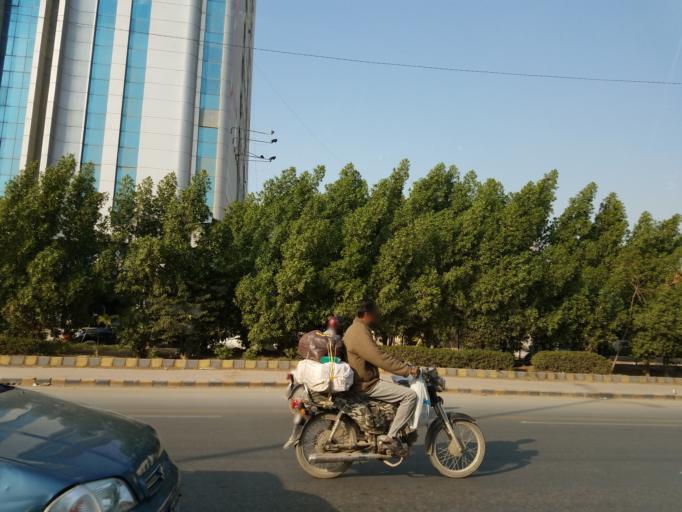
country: PK
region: Sindh
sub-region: Karachi District
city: Karachi
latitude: 24.8598
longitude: 67.0574
